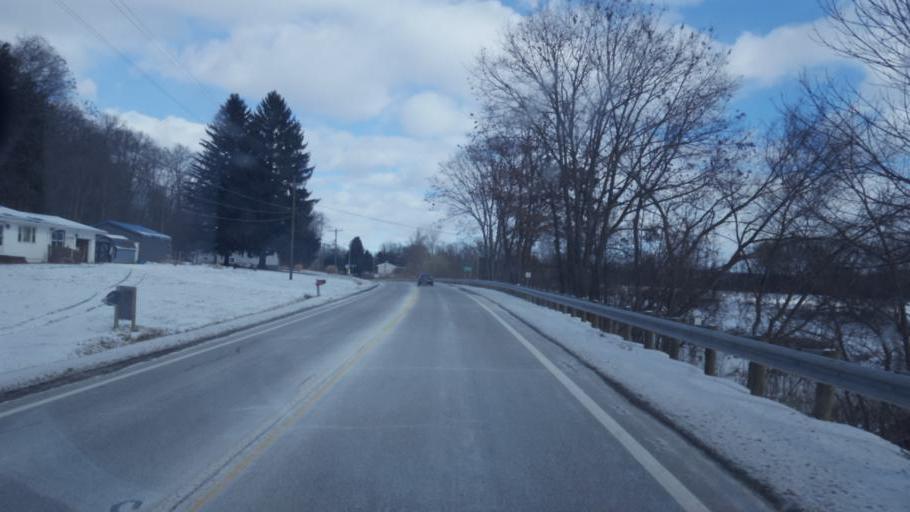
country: US
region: Ohio
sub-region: Coshocton County
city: Coshocton
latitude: 40.2104
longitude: -81.8828
